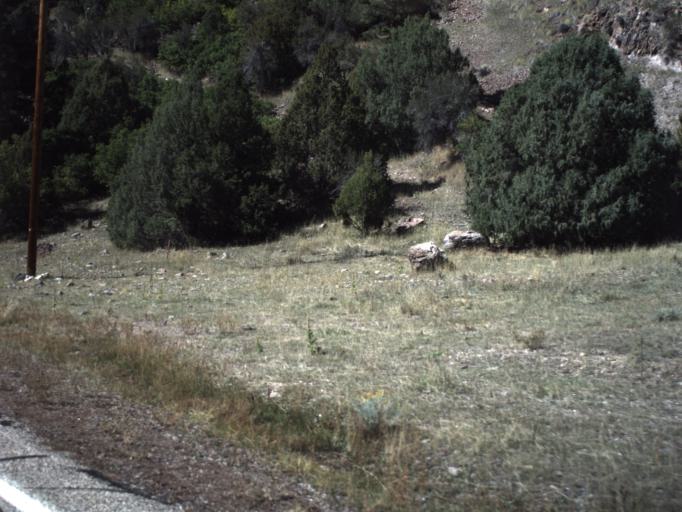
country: US
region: Utah
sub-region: Beaver County
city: Beaver
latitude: 38.2635
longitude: -112.4934
